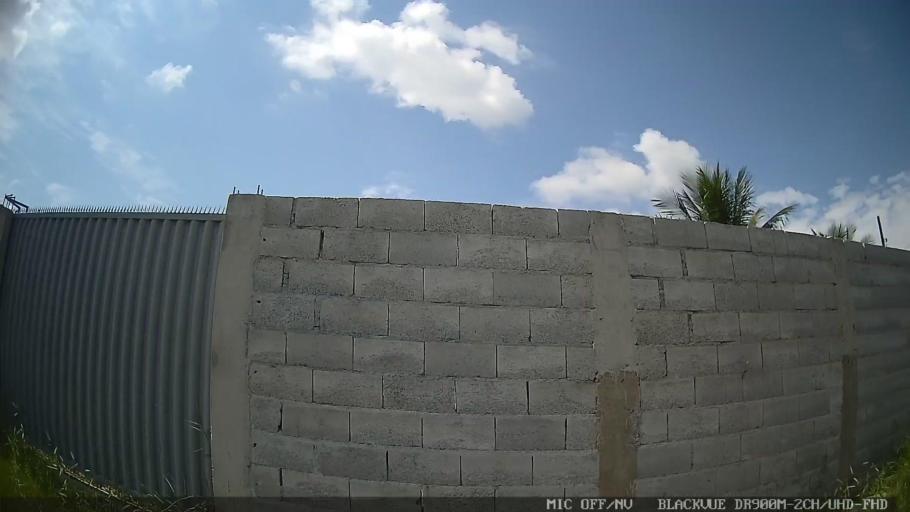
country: BR
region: Sao Paulo
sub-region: Caraguatatuba
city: Caraguatatuba
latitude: -23.6791
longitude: -45.4468
